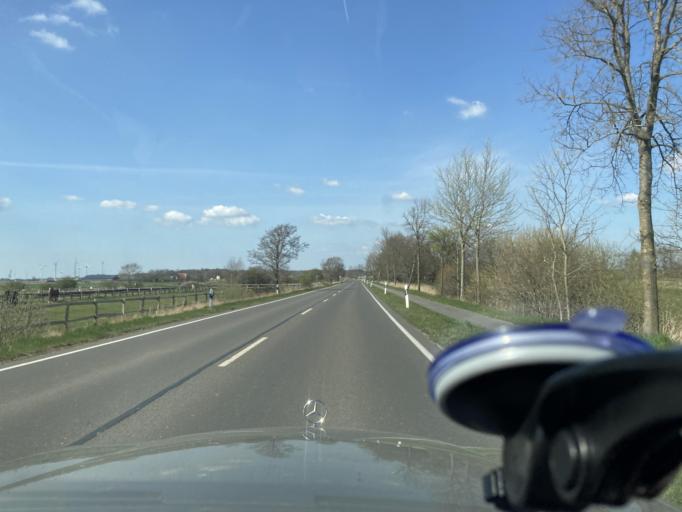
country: DE
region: Schleswig-Holstein
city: Stelle-Wittenwurth
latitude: 54.2550
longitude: 9.0599
